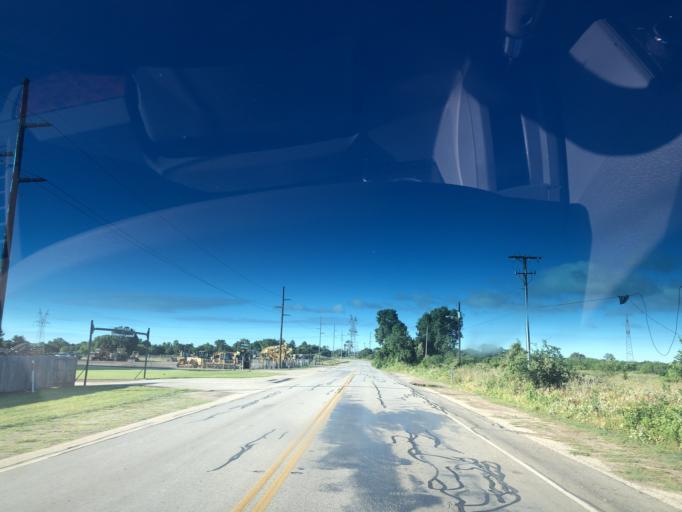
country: US
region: Texas
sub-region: Dallas County
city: Grand Prairie
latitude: 32.7892
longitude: -97.0172
